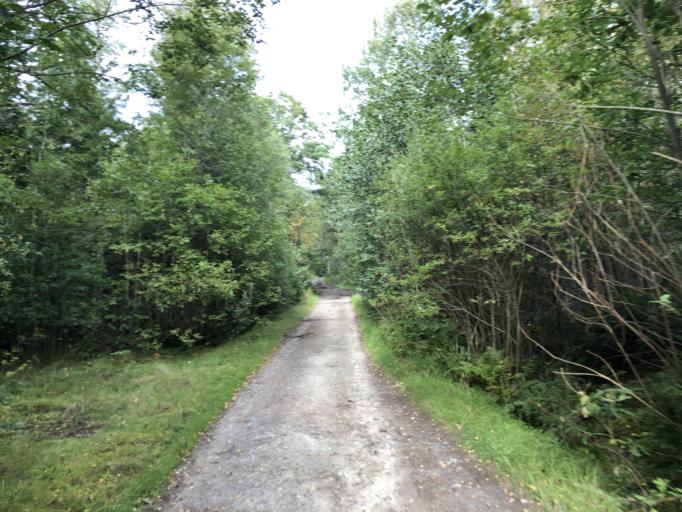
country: SE
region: Vaestra Goetaland
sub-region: Goteborg
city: Majorna
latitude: 57.7478
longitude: 11.8653
